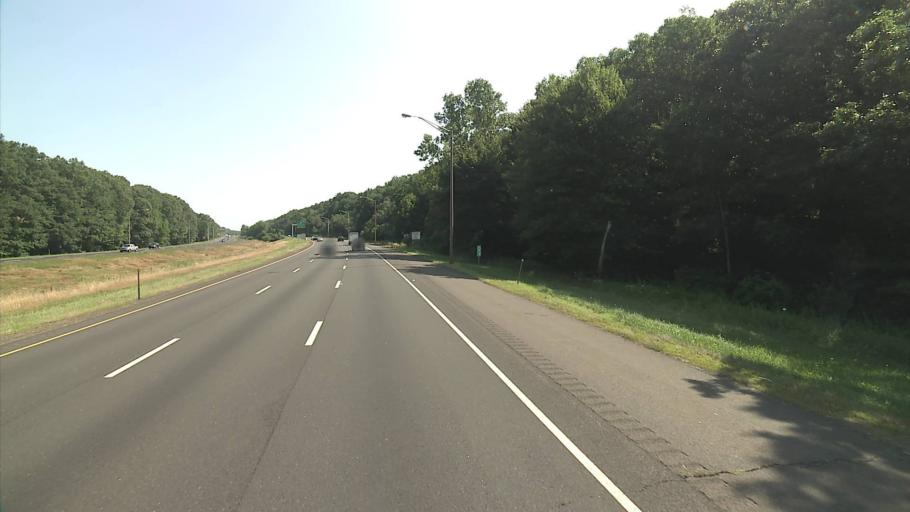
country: US
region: Connecticut
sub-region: New Haven County
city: North Haven
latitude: 41.4050
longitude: -72.8348
